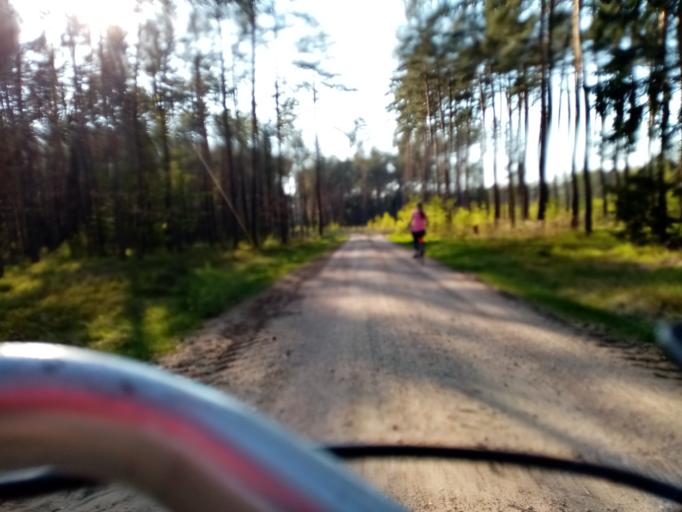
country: PL
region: Kujawsko-Pomorskie
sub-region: Powiat brodnicki
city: Gorzno
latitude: 53.1589
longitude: 19.6903
